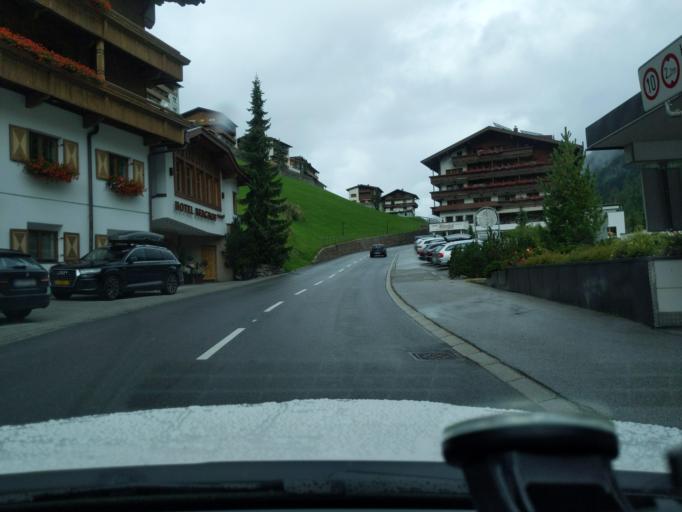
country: AT
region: Tyrol
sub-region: Politischer Bezirk Innsbruck Land
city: Schmirn
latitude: 47.1151
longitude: 11.6827
